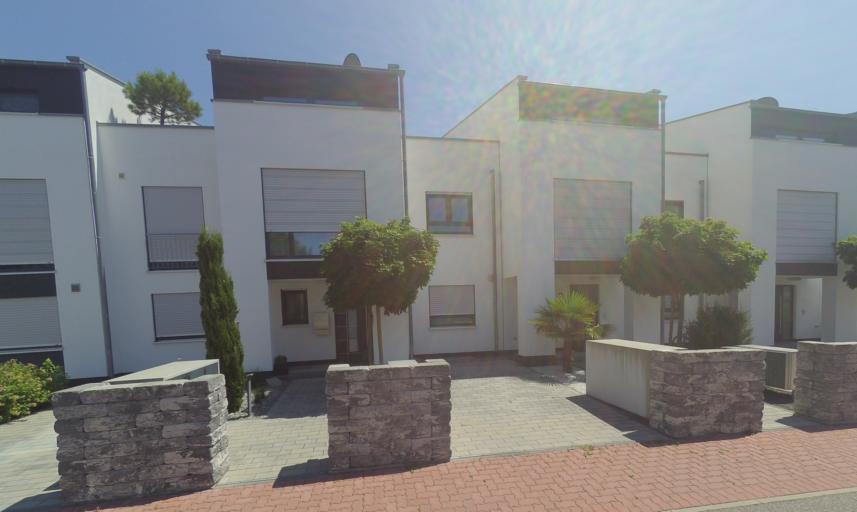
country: DE
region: Rheinland-Pfalz
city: Limburgerhof
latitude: 49.4278
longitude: 8.3966
